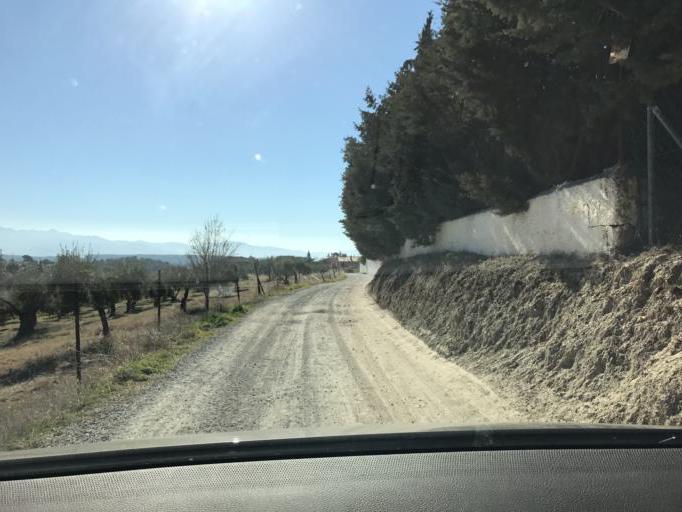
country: ES
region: Andalusia
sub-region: Provincia de Granada
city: Viznar
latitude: 37.2145
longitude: -3.5552
